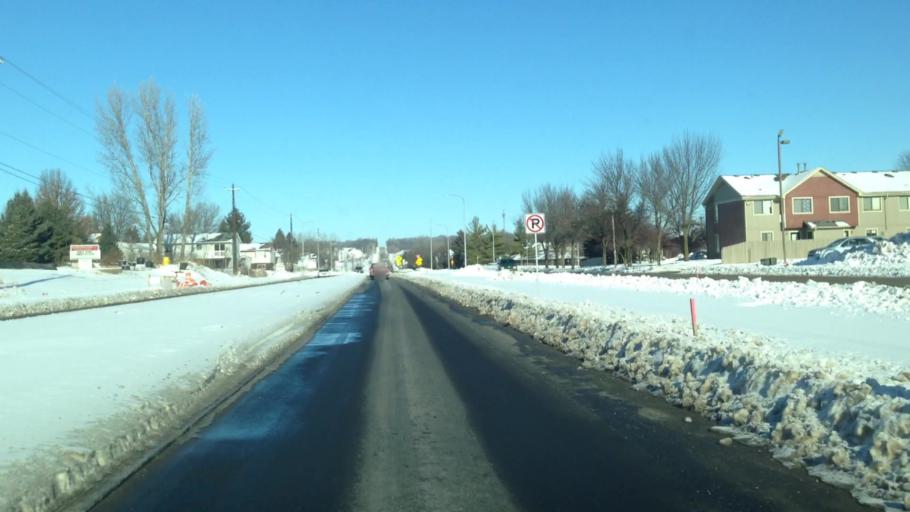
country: US
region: Minnesota
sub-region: Olmsted County
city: Rochester
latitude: 44.0700
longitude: -92.4888
